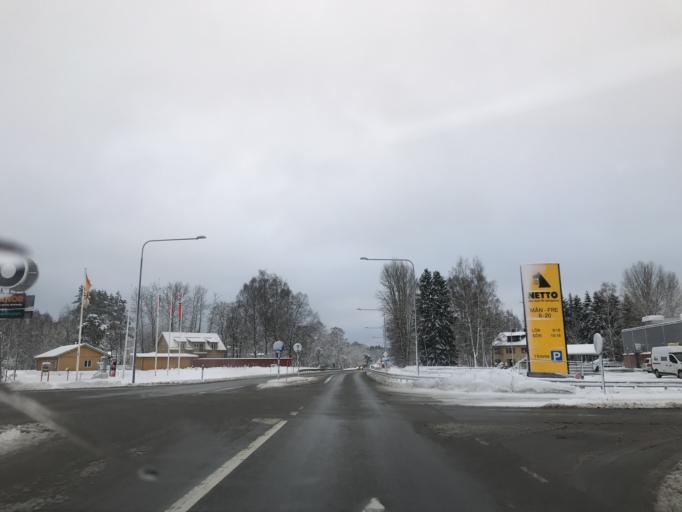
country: SE
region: Vaestra Goetaland
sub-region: Svenljunga Kommun
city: Svenljunga
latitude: 57.5006
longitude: 13.1135
